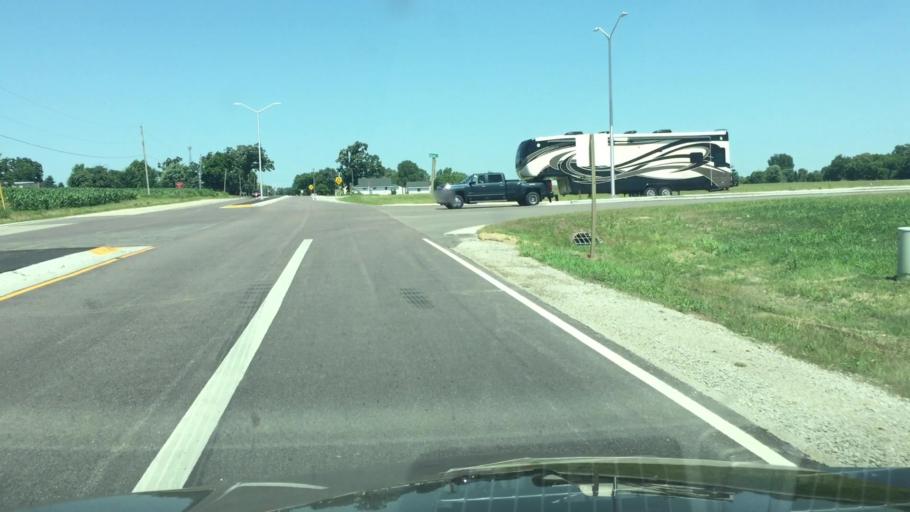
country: US
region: Wisconsin
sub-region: Fond du Lac County
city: Waupun
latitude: 43.6076
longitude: -88.7248
